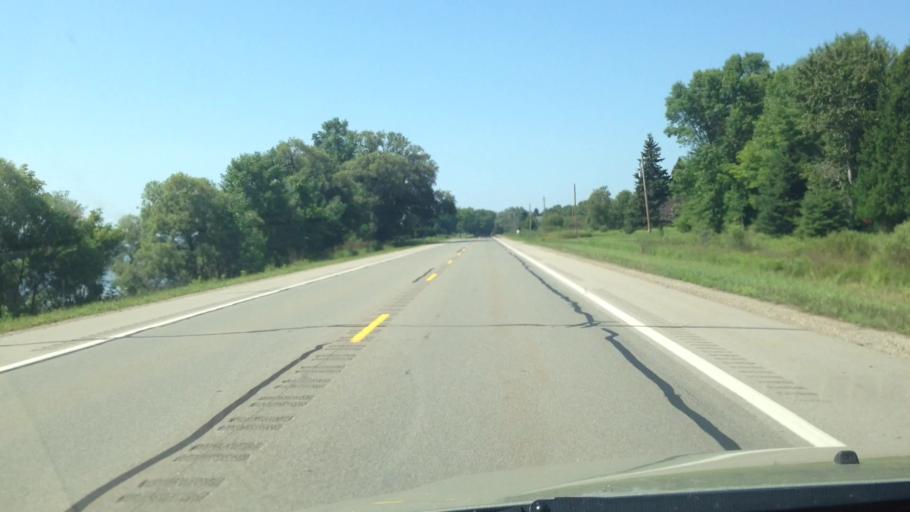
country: US
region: Michigan
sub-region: Menominee County
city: Menominee
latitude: 45.2491
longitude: -87.4889
